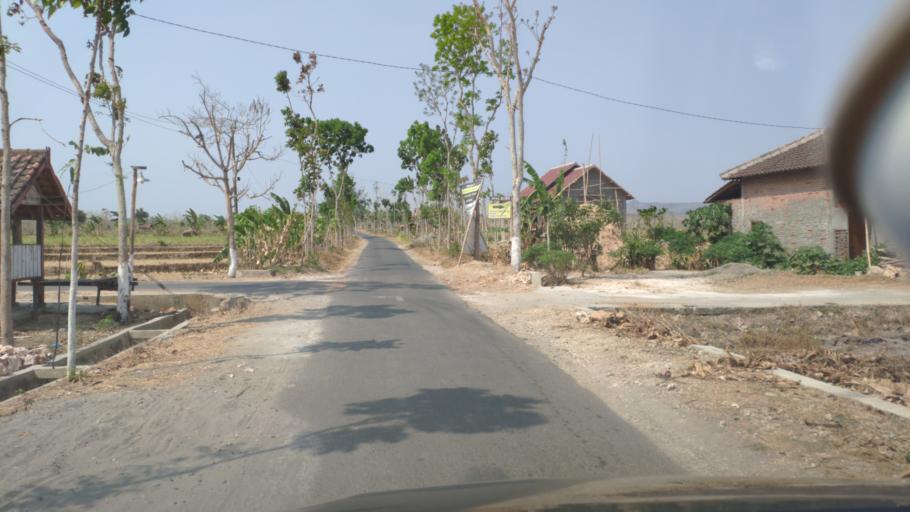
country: ID
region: Central Java
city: Karanggeneng
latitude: -6.9214
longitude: 111.4514
